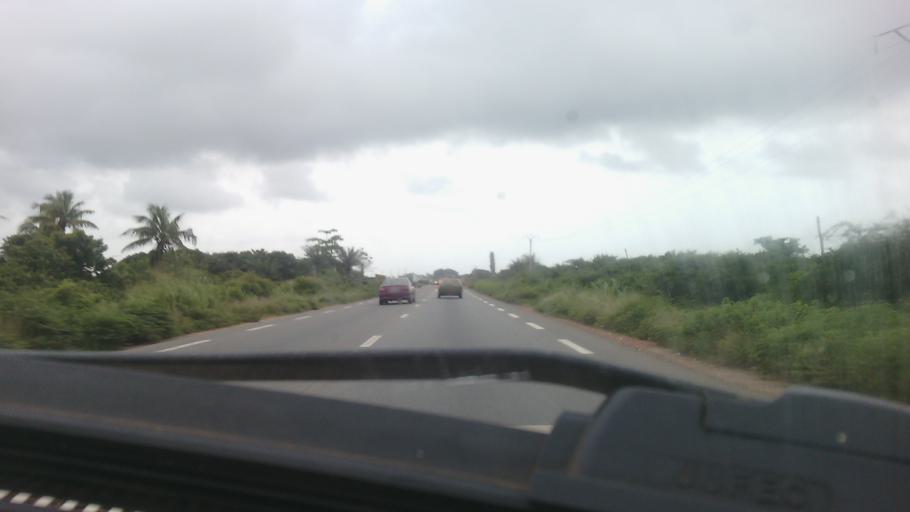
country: BJ
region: Atlantique
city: Ouidah
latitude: 6.3663
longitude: 2.0462
